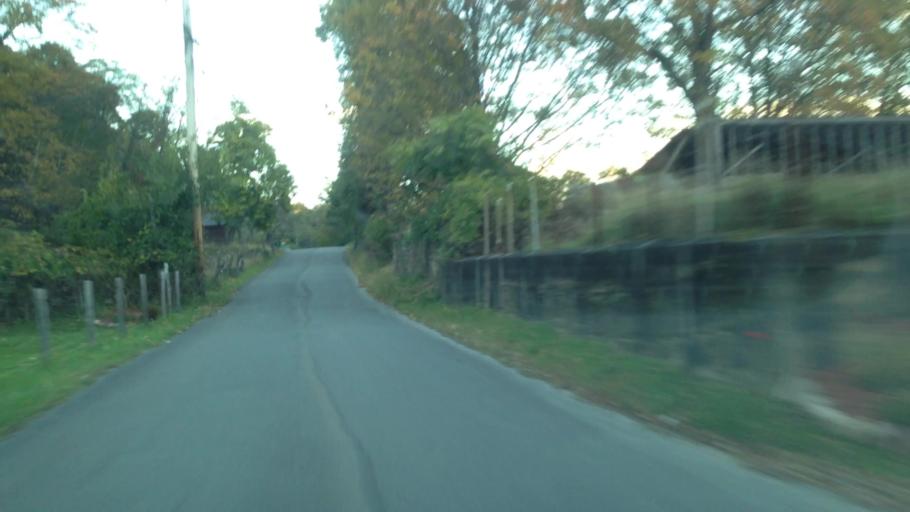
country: US
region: New York
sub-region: Dutchess County
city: Hyde Park
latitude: 41.8238
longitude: -73.9884
